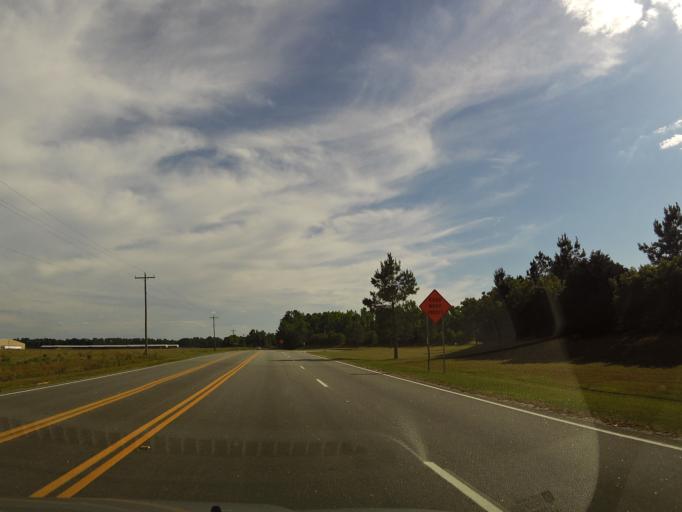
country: US
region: South Carolina
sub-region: Allendale County
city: Fairfax
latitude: 32.9901
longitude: -81.2236
